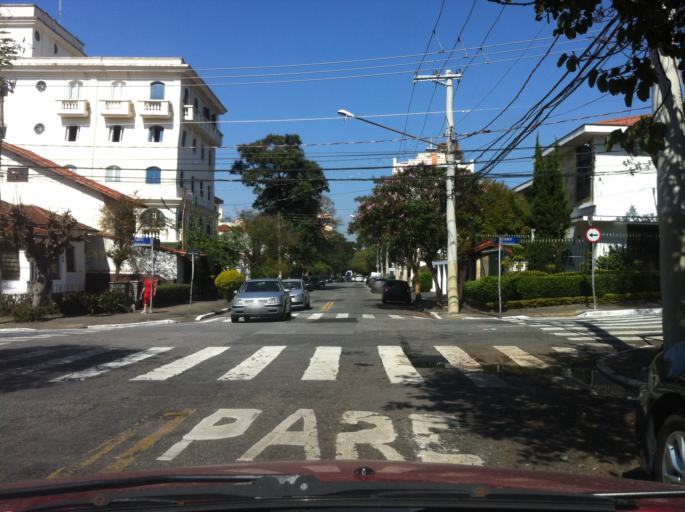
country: BR
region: Sao Paulo
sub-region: Diadema
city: Diadema
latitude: -23.6248
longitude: -46.6444
